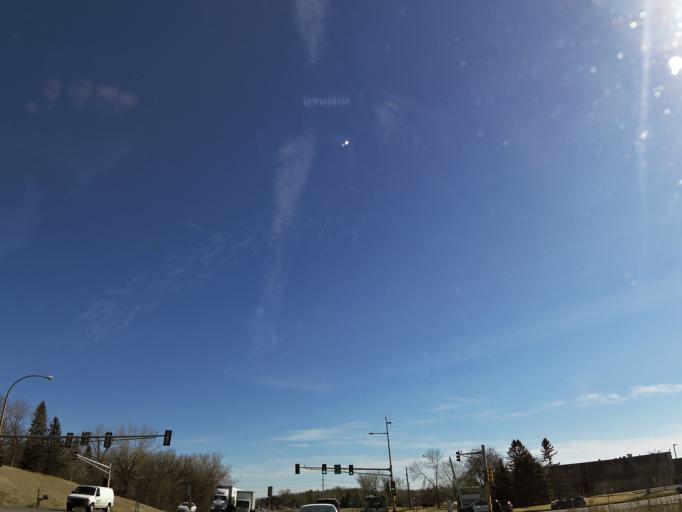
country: US
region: Minnesota
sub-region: Hennepin County
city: Plymouth
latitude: 45.0001
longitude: -93.4424
